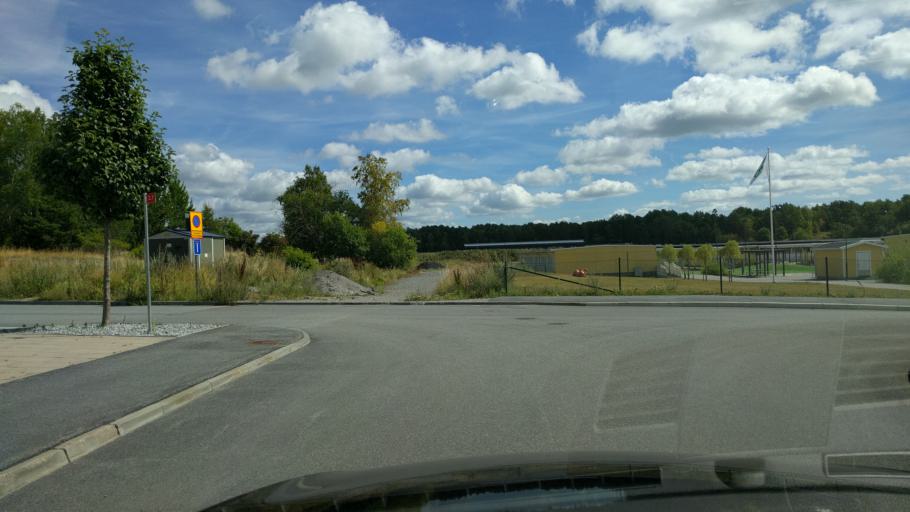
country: SE
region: Stockholm
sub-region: Jarfalla Kommun
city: Jakobsberg
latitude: 59.4175
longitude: 17.8679
